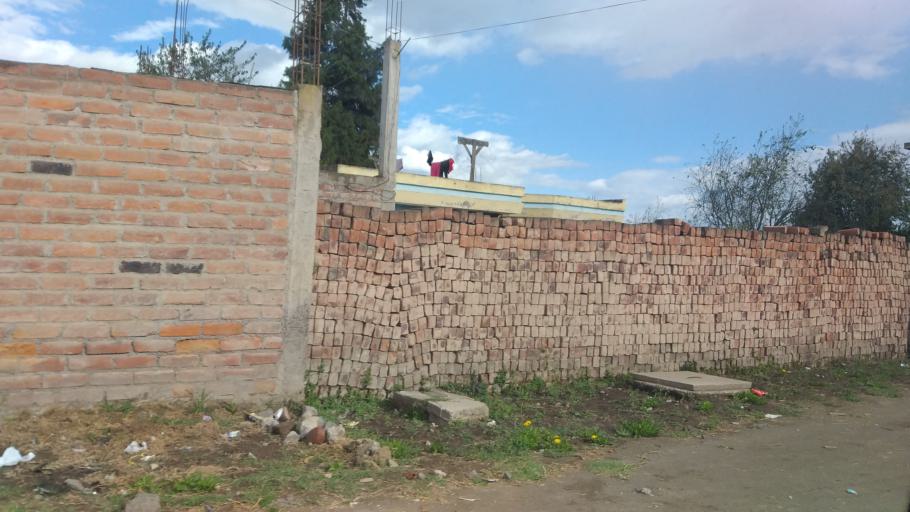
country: EC
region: Chimborazo
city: Riobamba
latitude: -1.6856
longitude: -78.6261
